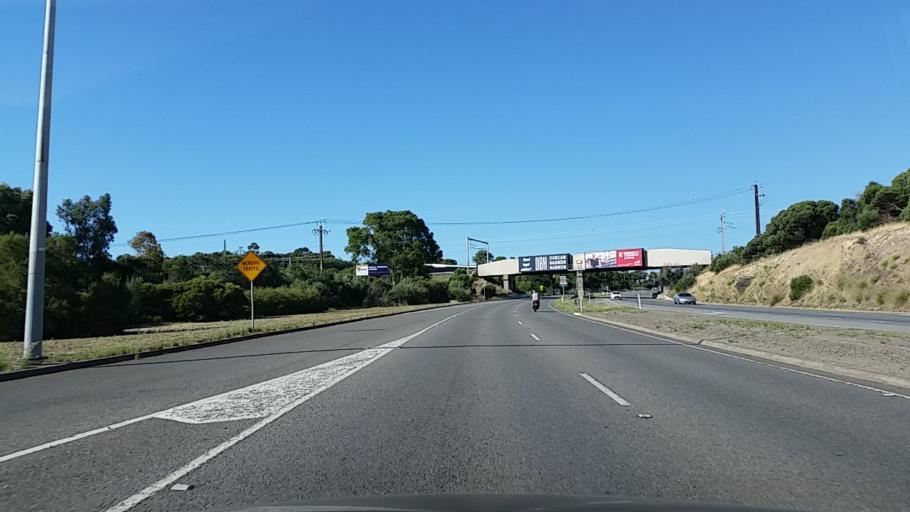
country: AU
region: South Australia
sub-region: Onkaparinga
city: Morphett Vale
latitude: -35.1129
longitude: 138.4920
